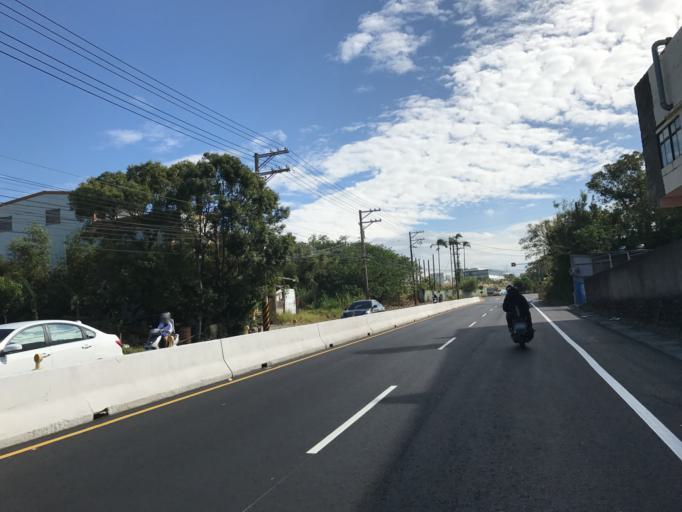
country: TW
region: Taiwan
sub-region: Hsinchu
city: Zhubei
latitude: 24.7786
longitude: 121.0440
